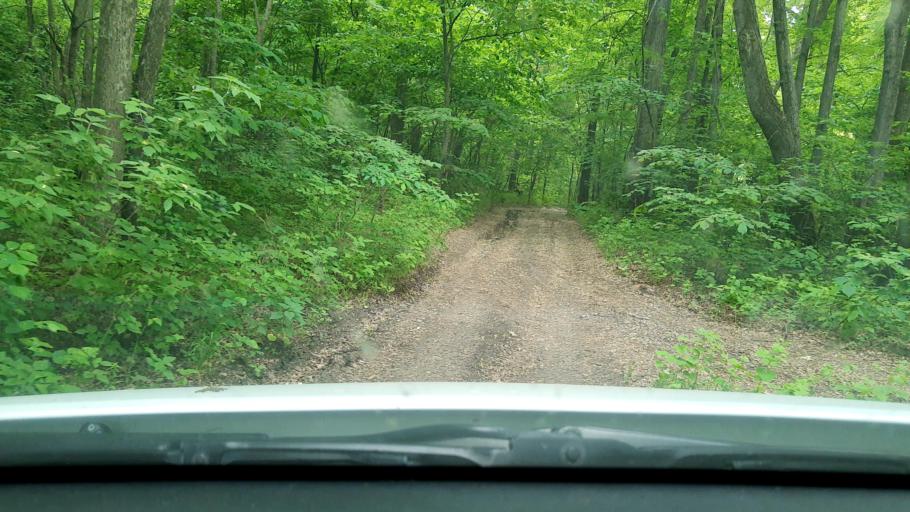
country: RU
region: Bashkortostan
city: Ufa
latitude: 54.6596
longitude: 55.8755
